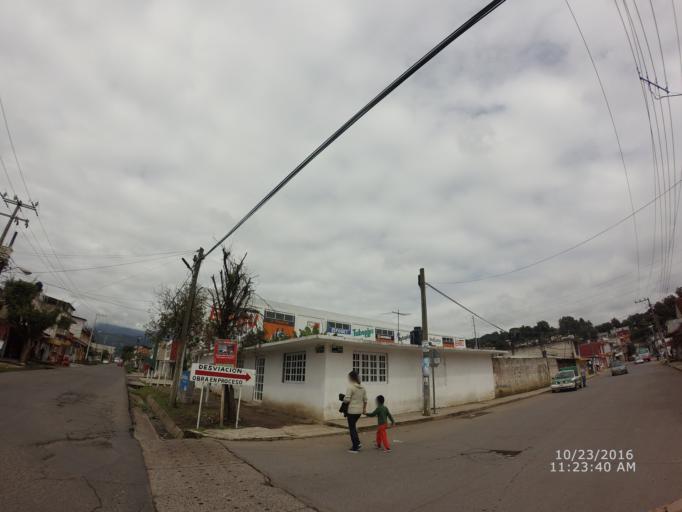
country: MX
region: Veracruz
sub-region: Tlalnelhuayocan
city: Guadalupe Victoria
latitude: 19.5512
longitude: -96.9502
